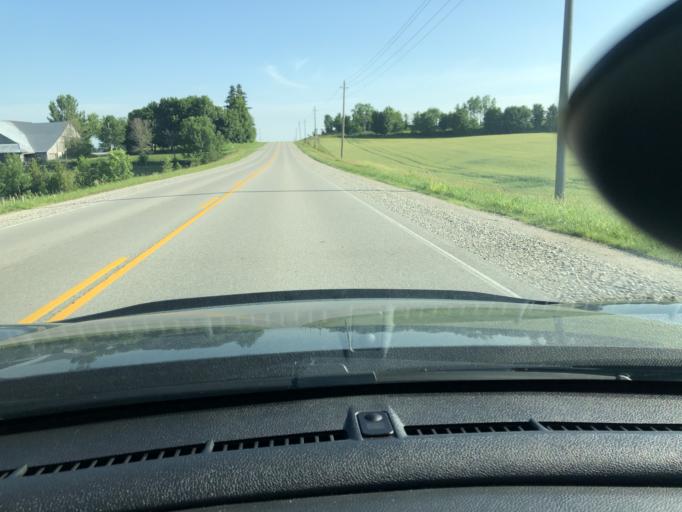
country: CA
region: Ontario
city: Stratford
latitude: 43.4093
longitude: -80.8377
